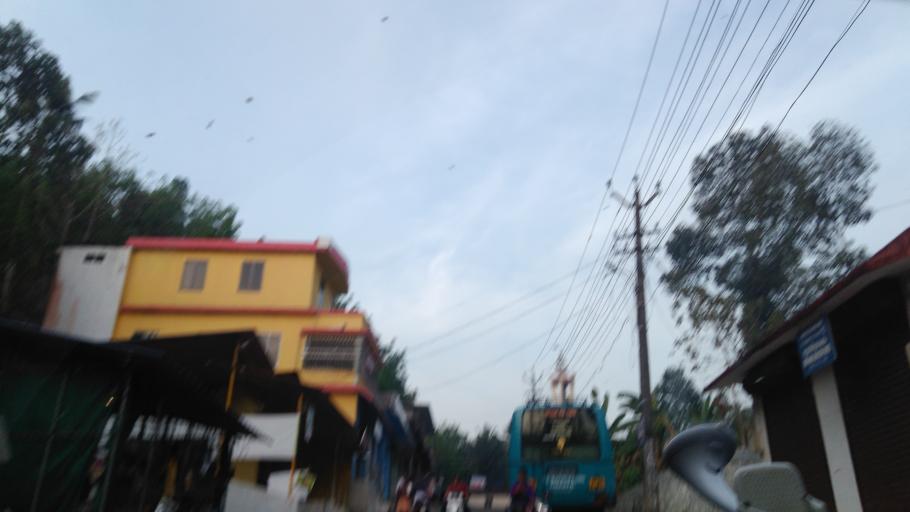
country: IN
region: Kerala
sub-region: Kottayam
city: Palackattumala
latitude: 9.8464
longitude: 76.6509
